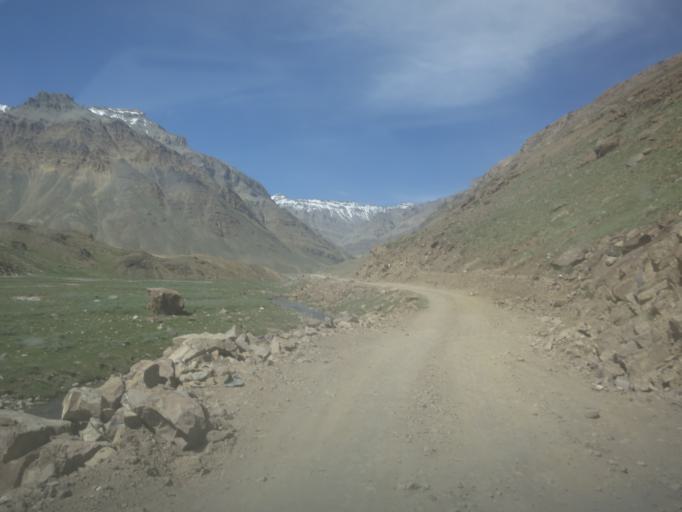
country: IN
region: Himachal Pradesh
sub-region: Kulu
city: Manali
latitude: 32.4455
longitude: 77.6910
